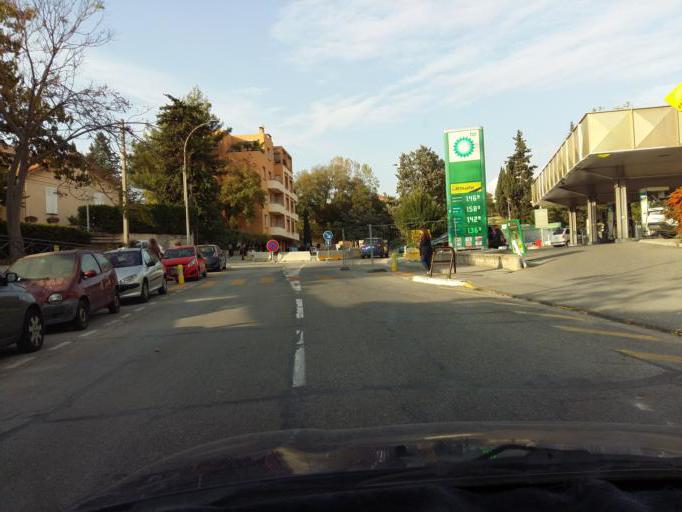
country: FR
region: Provence-Alpes-Cote d'Azur
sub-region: Departement des Bouches-du-Rhone
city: Aix-en-Provence
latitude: 43.5201
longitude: 5.4469
